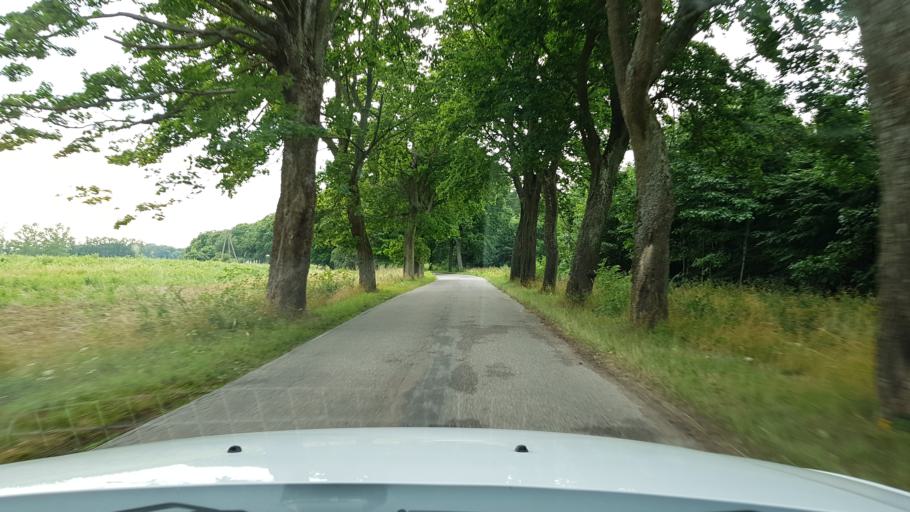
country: PL
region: West Pomeranian Voivodeship
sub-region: Powiat drawski
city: Wierzchowo
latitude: 53.4746
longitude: 16.0676
